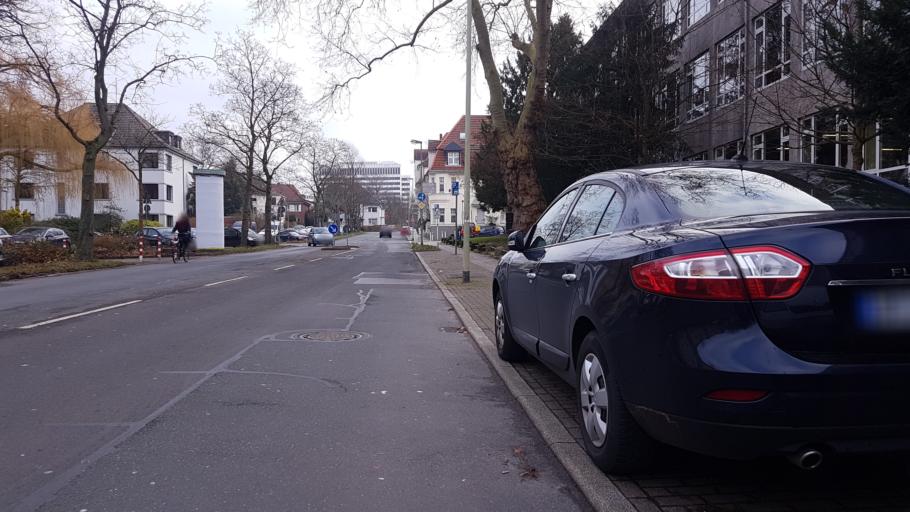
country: DE
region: North Rhine-Westphalia
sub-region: Regierungsbezirk Dusseldorf
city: Essen
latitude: 51.4435
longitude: 7.0263
